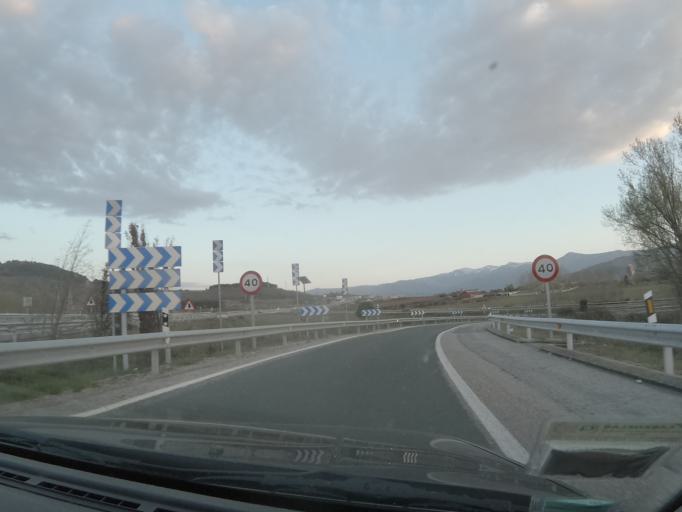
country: ES
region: Castille and Leon
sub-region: Provincia de Leon
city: Ponferrada
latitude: 42.5804
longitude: -6.6061
